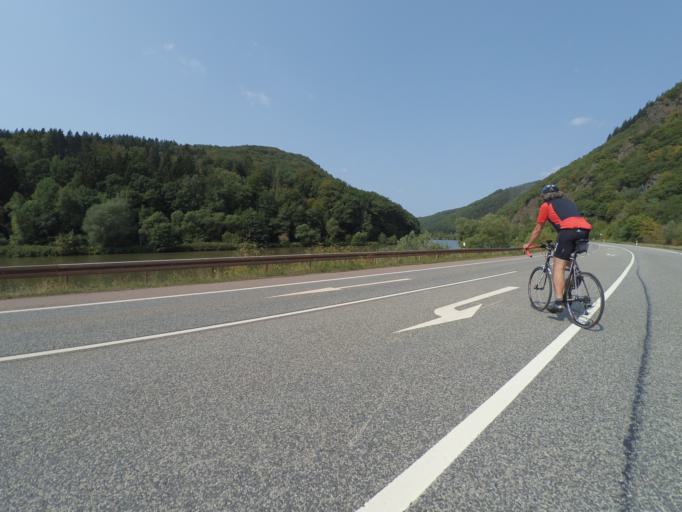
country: DE
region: Saarland
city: Saarhoelzbach
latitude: 49.5203
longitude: 6.6113
